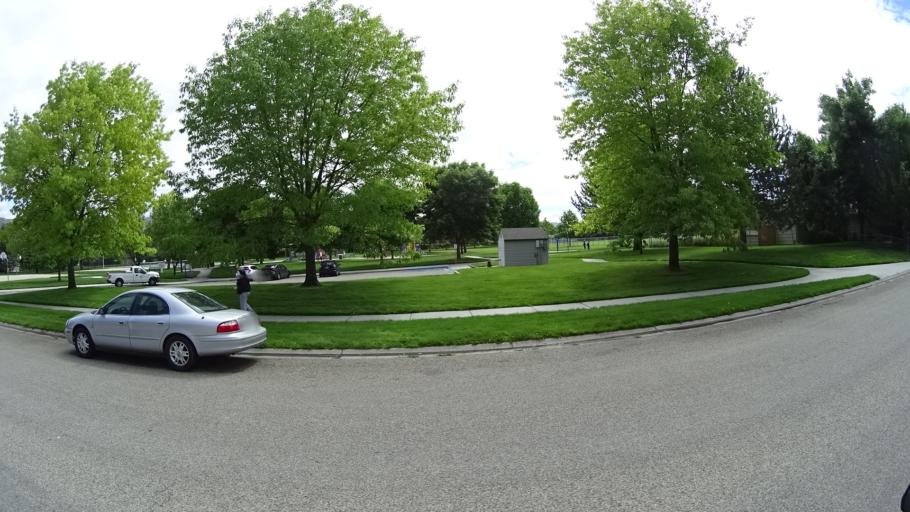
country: US
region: Idaho
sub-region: Ada County
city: Boise
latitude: 43.5706
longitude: -116.1635
